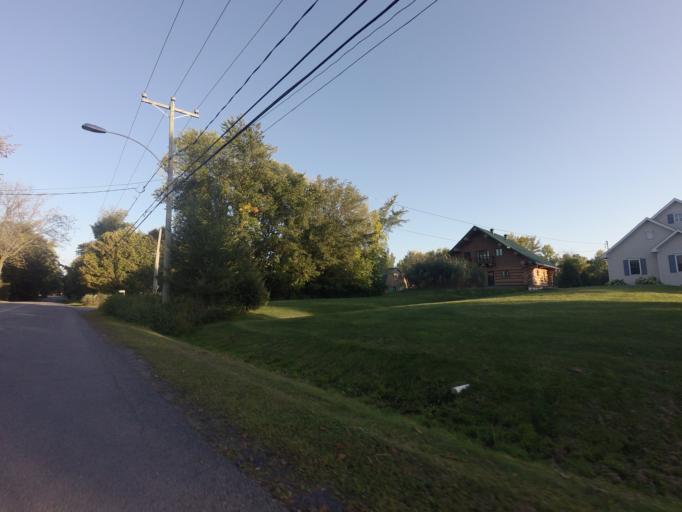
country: CA
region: Quebec
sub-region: Monteregie
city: Rigaud
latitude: 45.4786
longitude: -74.2393
